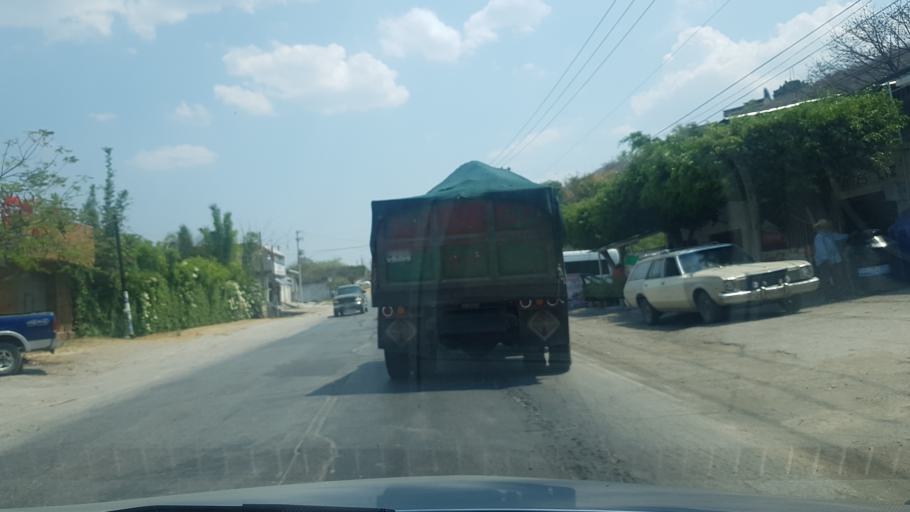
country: MX
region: Morelos
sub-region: Tlaltizapan de Zapata
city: Colonia Palo Prieto (Chipitongo)
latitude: 18.7132
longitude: -99.1181
